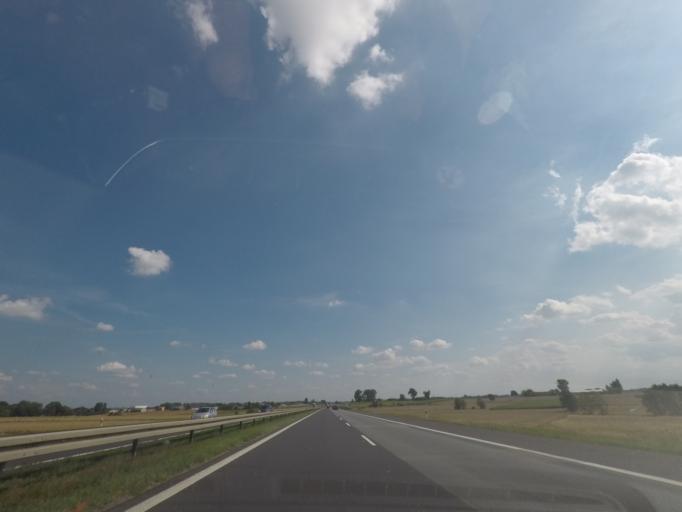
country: PL
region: Lodz Voivodeship
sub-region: Powiat piotrkowski
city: Moszczenica
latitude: 51.4744
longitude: 19.6285
